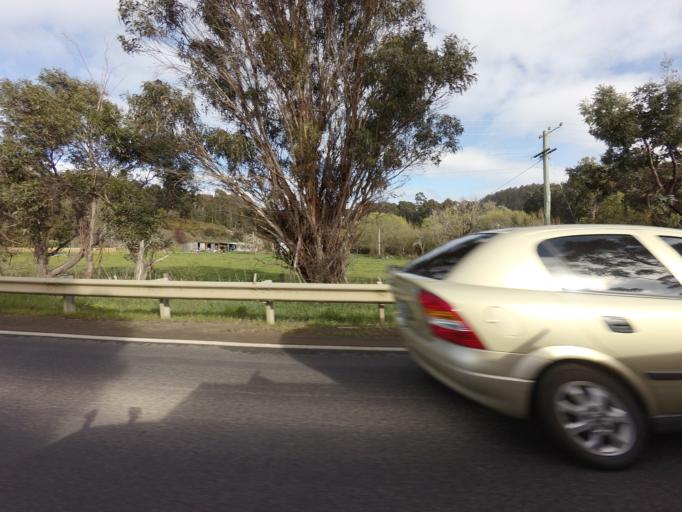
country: AU
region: Tasmania
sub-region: Huon Valley
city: Franklin
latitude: -43.0674
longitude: 147.0246
